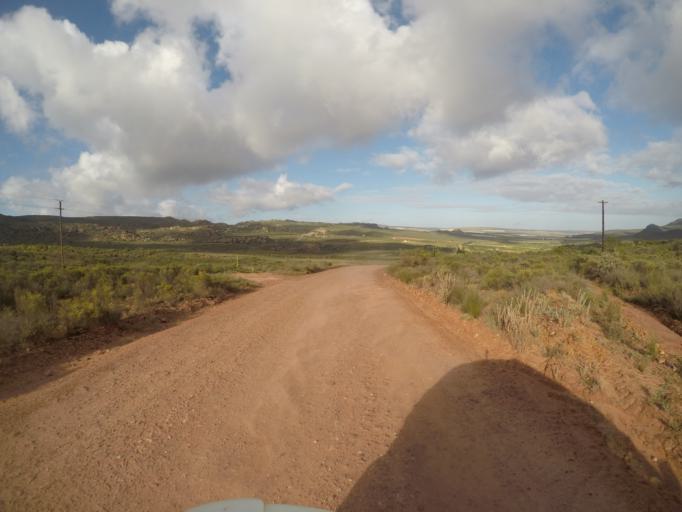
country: ZA
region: Western Cape
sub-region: West Coast District Municipality
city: Clanwilliam
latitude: -32.3436
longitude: 18.7569
